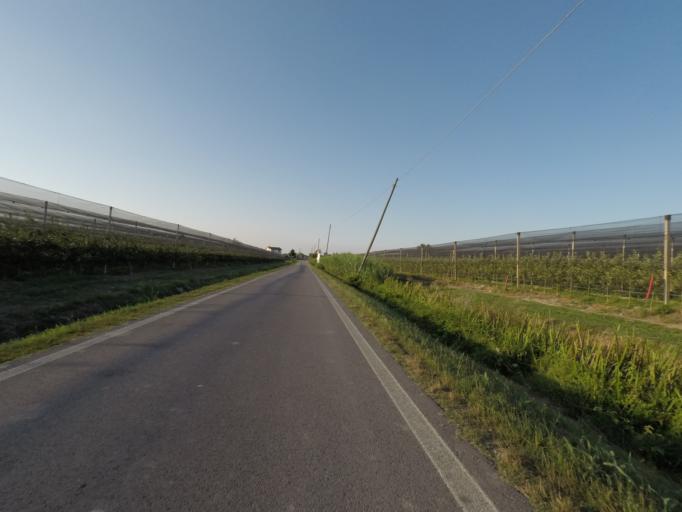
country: IT
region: Veneto
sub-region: Provincia di Rovigo
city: Fratta Polesine
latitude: 45.0371
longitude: 11.6696
